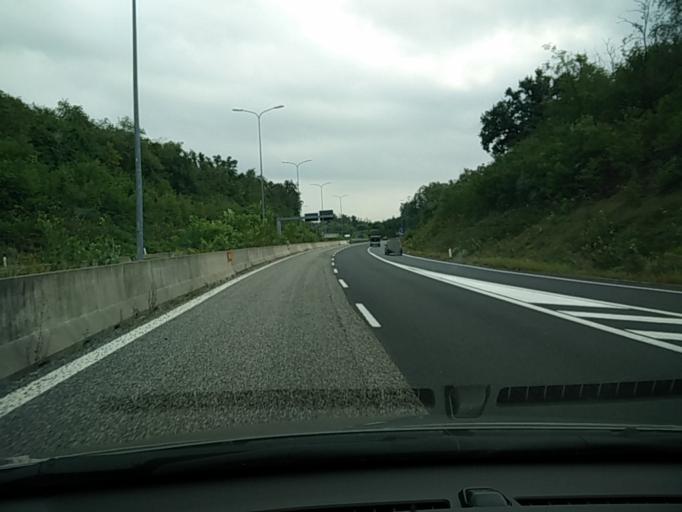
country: IT
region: Lombardy
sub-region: Provincia di Varese
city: Lonate Pozzolo
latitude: 45.5830
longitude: 8.7273
